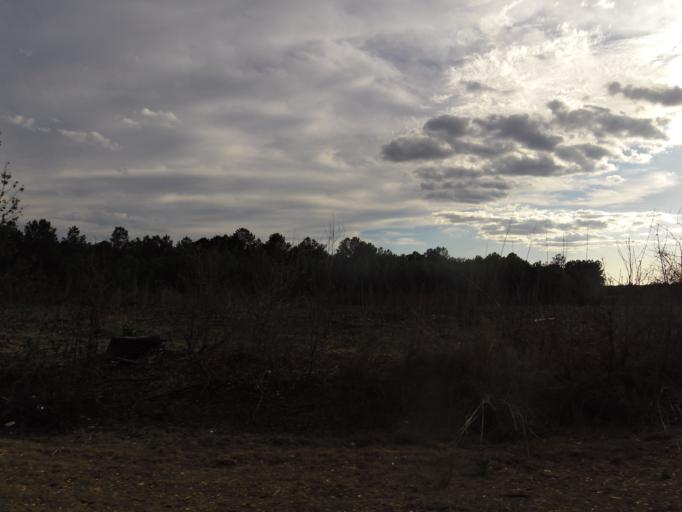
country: US
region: South Carolina
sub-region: Jasper County
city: Ridgeland
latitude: 32.4961
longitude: -81.1293
